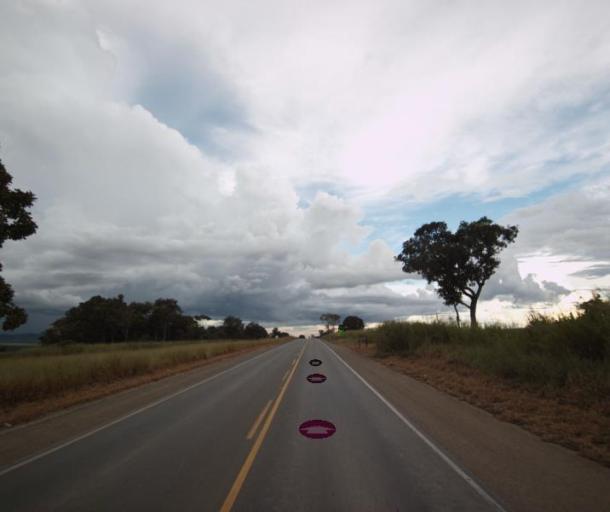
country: BR
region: Goias
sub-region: Itapaci
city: Itapaci
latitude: -14.8396
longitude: -49.3098
